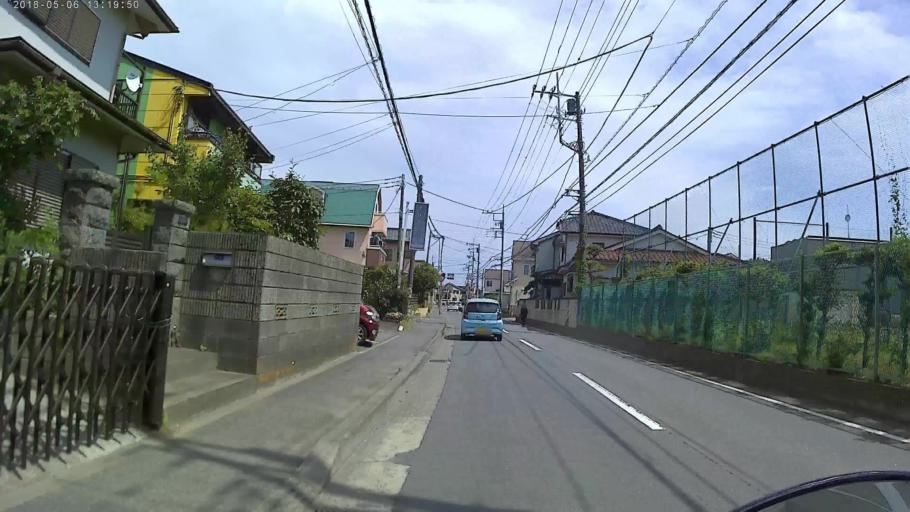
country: JP
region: Kanagawa
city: Minami-rinkan
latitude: 35.4127
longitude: 139.4430
